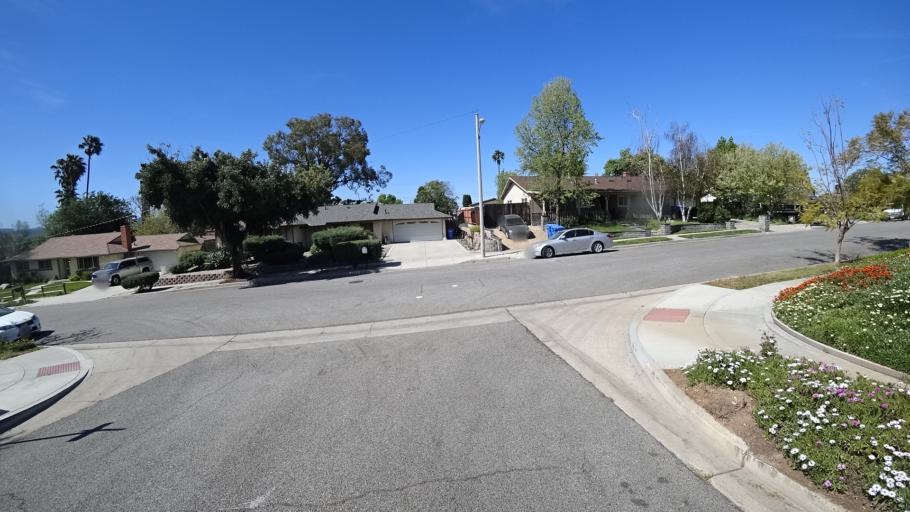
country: US
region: California
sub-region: Ventura County
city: Thousand Oaks
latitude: 34.2192
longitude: -118.8612
